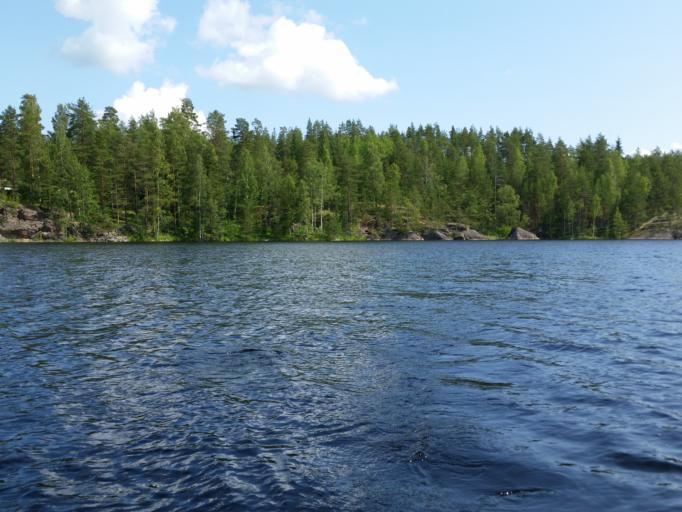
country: FI
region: Southern Savonia
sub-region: Savonlinna
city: Sulkava
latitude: 61.7698
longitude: 28.4382
